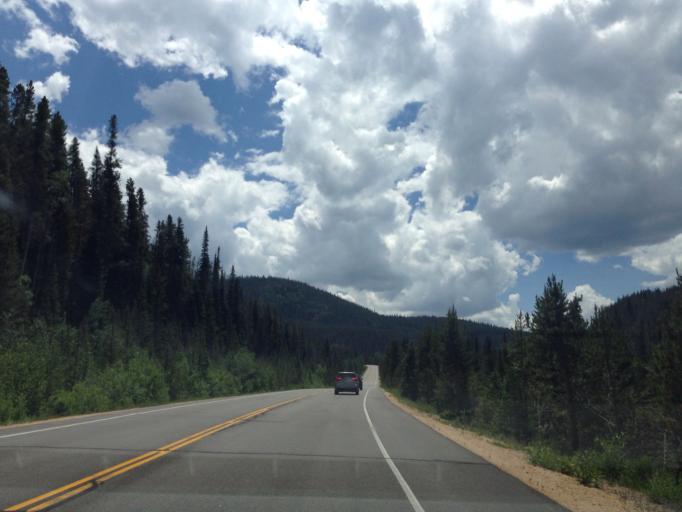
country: US
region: Colorado
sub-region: Larimer County
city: Estes Park
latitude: 40.6227
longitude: -105.8166
